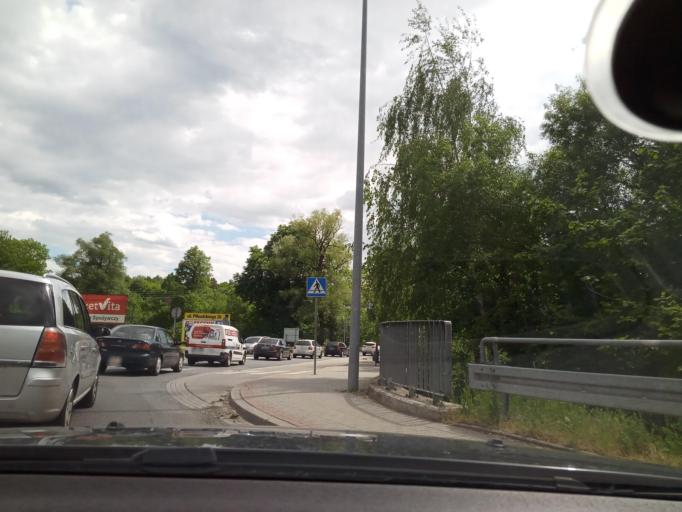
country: PL
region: Lesser Poland Voivodeship
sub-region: Powiat limanowski
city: Limanowa
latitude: 49.7363
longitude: 20.4013
